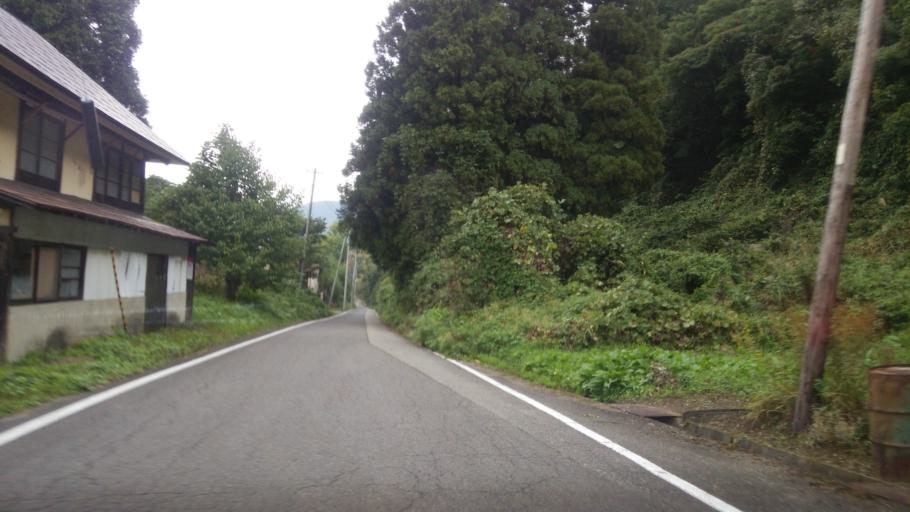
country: JP
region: Fukushima
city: Inawashiro
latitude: 37.3819
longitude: 139.9289
